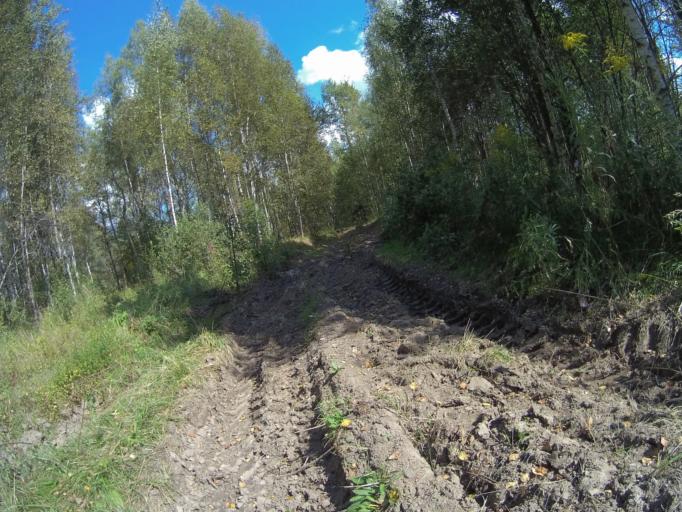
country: RU
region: Vladimir
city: Sudogda
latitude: 55.9274
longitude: 40.6764
